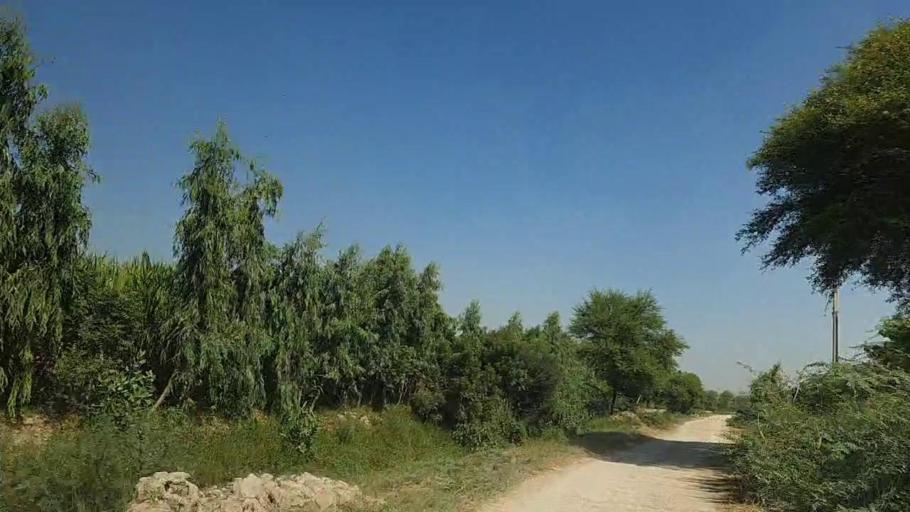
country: PK
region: Sindh
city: Daro Mehar
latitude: 24.7753
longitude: 68.1566
